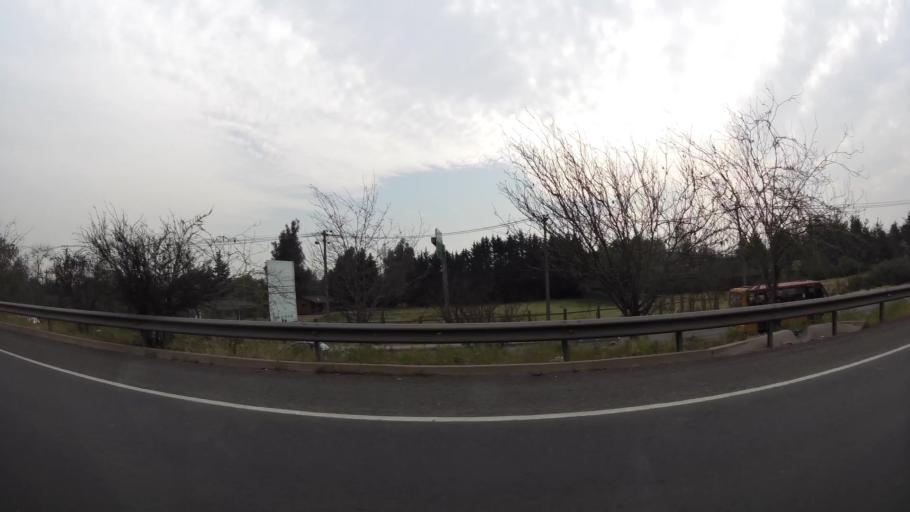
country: CL
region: Santiago Metropolitan
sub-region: Provincia de Chacabuco
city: Chicureo Abajo
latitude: -33.2396
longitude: -70.6974
